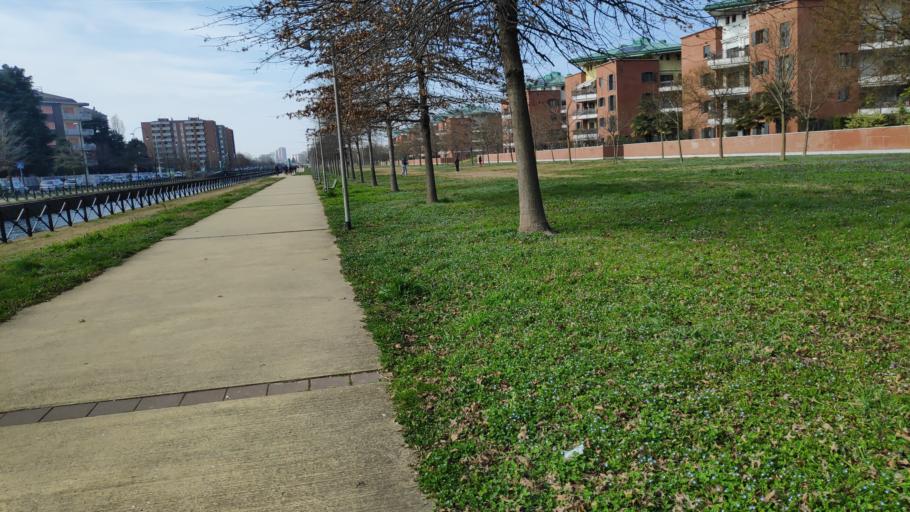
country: IT
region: Lombardy
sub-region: Citta metropolitana di Milano
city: Vimodrone
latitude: 45.5175
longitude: 9.2821
